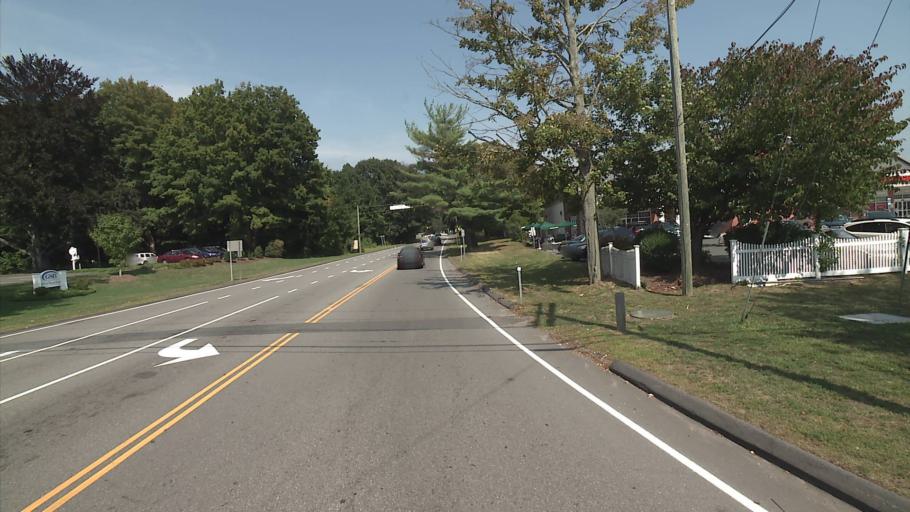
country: US
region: Connecticut
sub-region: New Haven County
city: Madison
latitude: 41.2794
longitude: -72.5985
